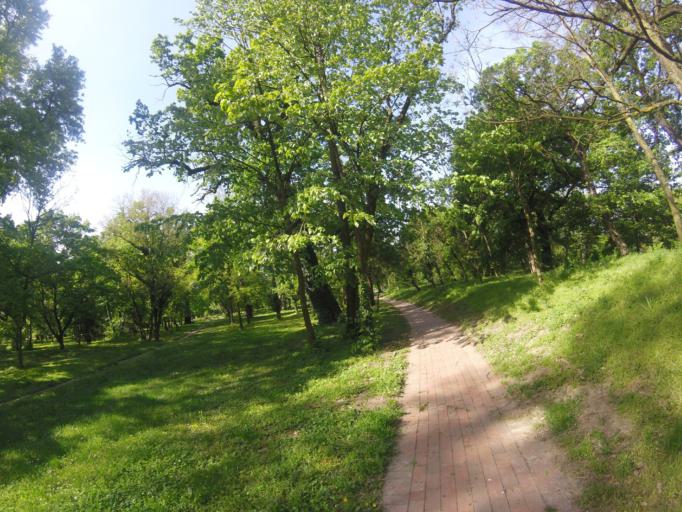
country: HU
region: Bekes
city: Doboz
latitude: 46.7389
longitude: 21.2457
